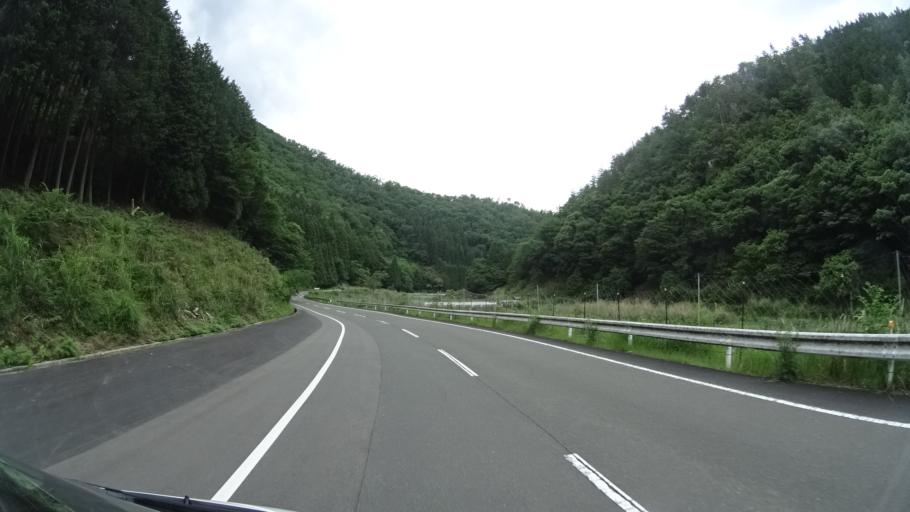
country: JP
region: Hyogo
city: Sasayama
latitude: 35.0607
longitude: 135.3926
